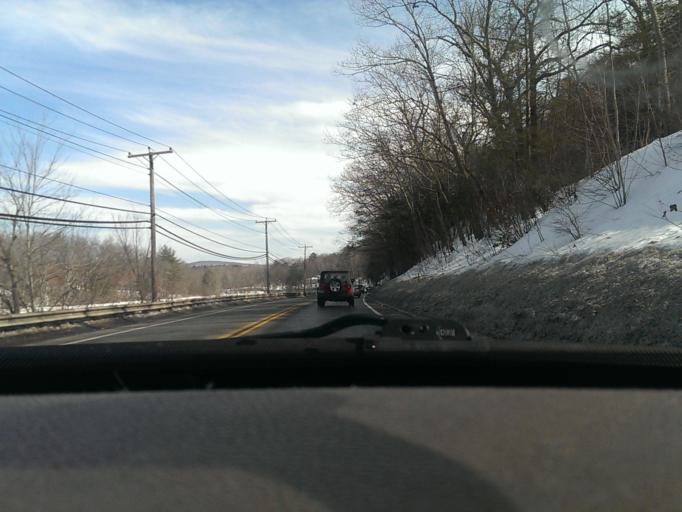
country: US
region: Massachusetts
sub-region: Hampden County
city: Wilbraham
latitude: 42.1543
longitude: -72.4181
